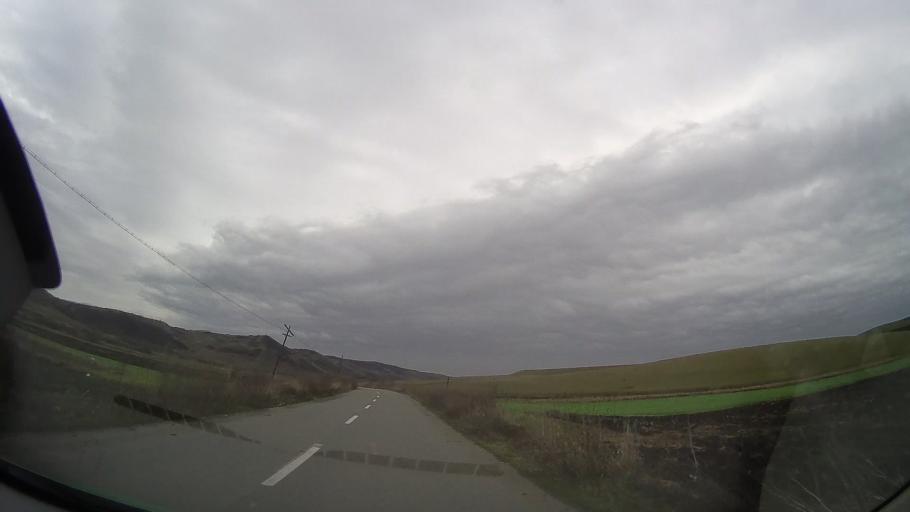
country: RO
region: Mures
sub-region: Comuna Craesti
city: Craiesti
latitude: 46.7877
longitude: 24.4229
